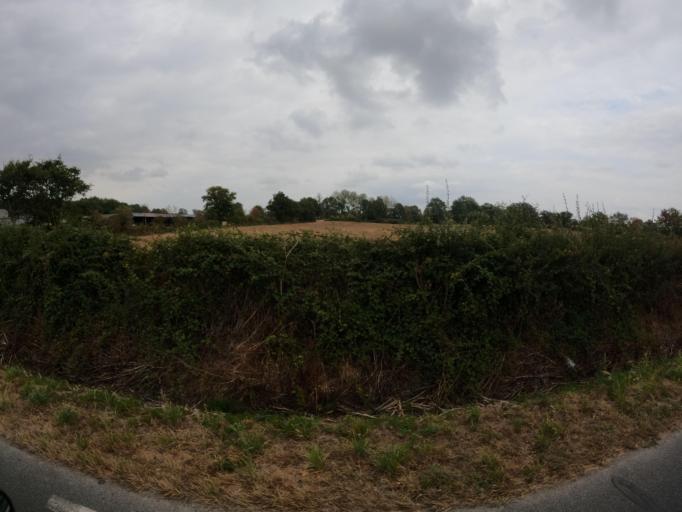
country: FR
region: Pays de la Loire
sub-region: Departement de la Vendee
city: Les Landes-Genusson
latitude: 46.9890
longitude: -1.1459
